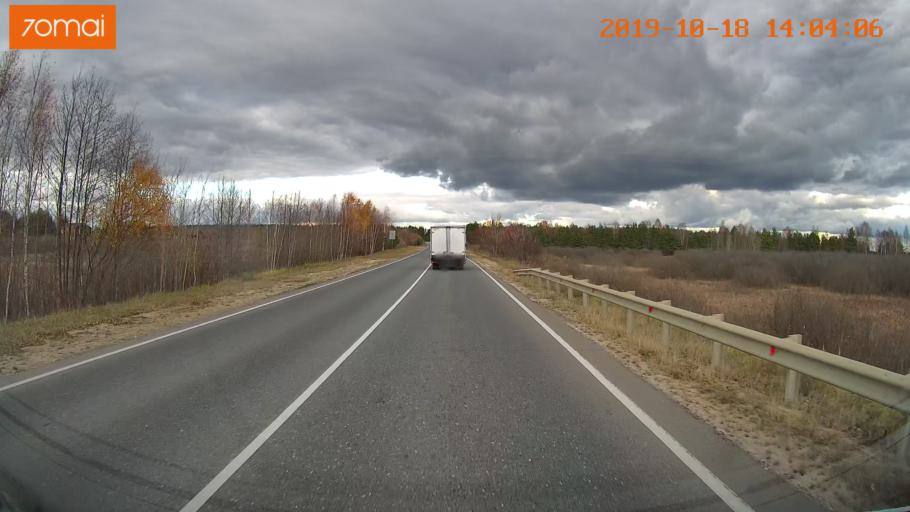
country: RU
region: Rjazan
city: Spas-Klepiki
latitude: 55.1224
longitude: 40.1334
